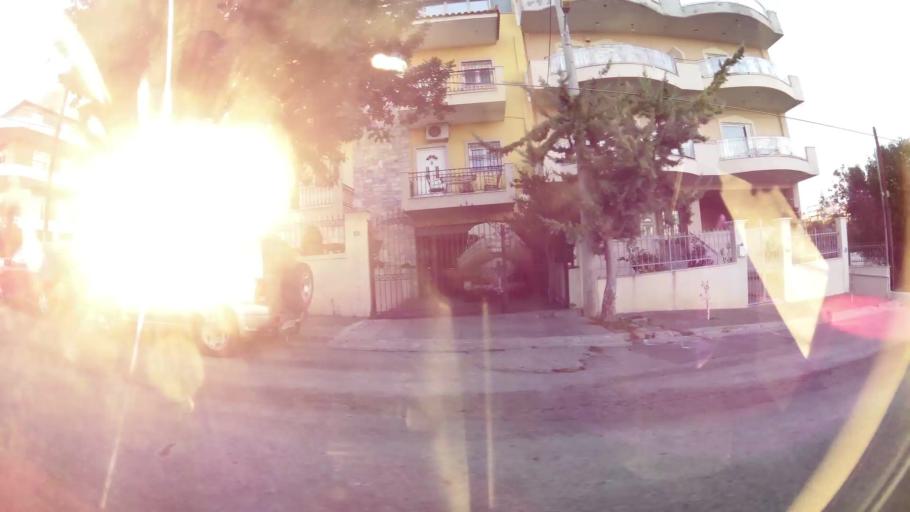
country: GR
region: Attica
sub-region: Nomarchia Anatolikis Attikis
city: Spata
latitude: 37.9592
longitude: 23.9266
